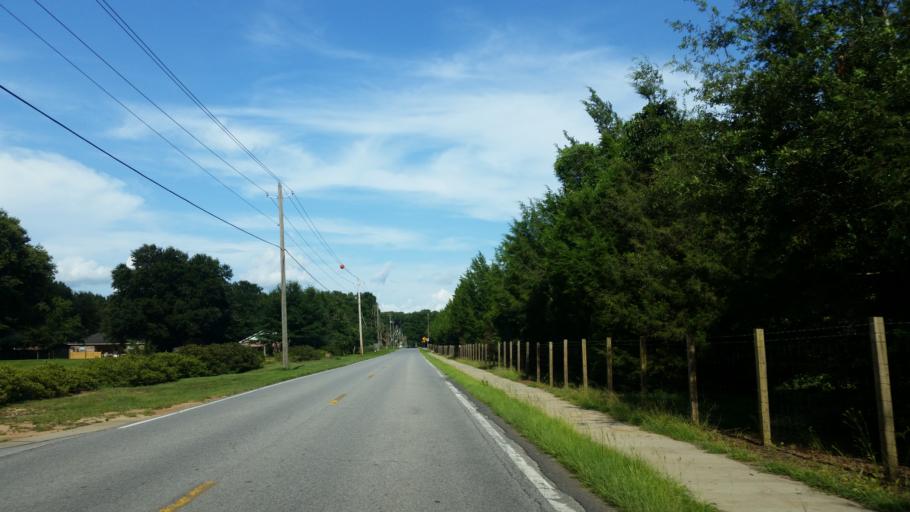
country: US
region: Florida
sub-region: Santa Rosa County
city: Pace
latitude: 30.6325
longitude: -87.1434
